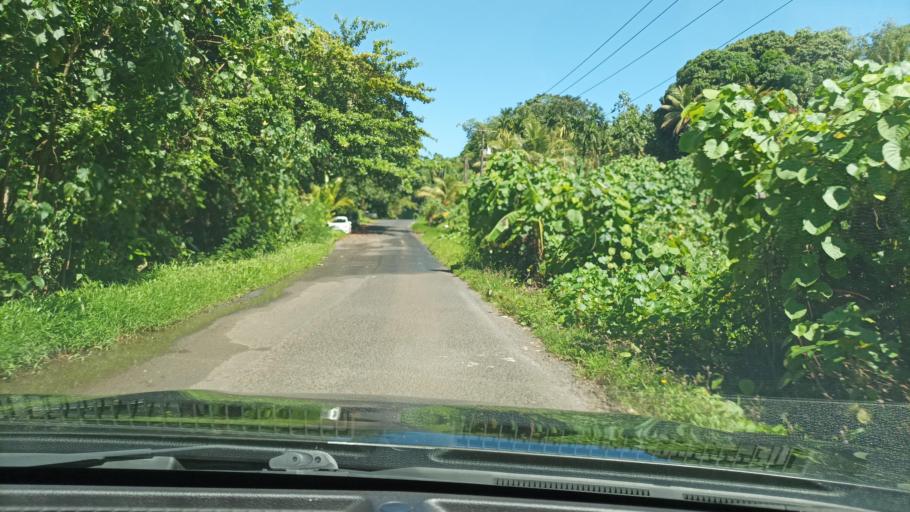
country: FM
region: Pohnpei
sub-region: Madolenihm Municipality
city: Madolenihm Municipality Government
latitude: 6.8509
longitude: 158.2982
